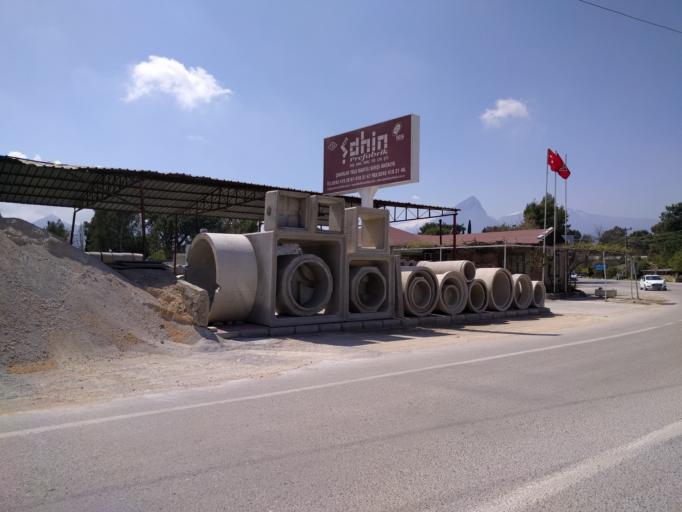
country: TR
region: Antalya
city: Cakirlar
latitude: 36.8949
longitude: 30.5975
